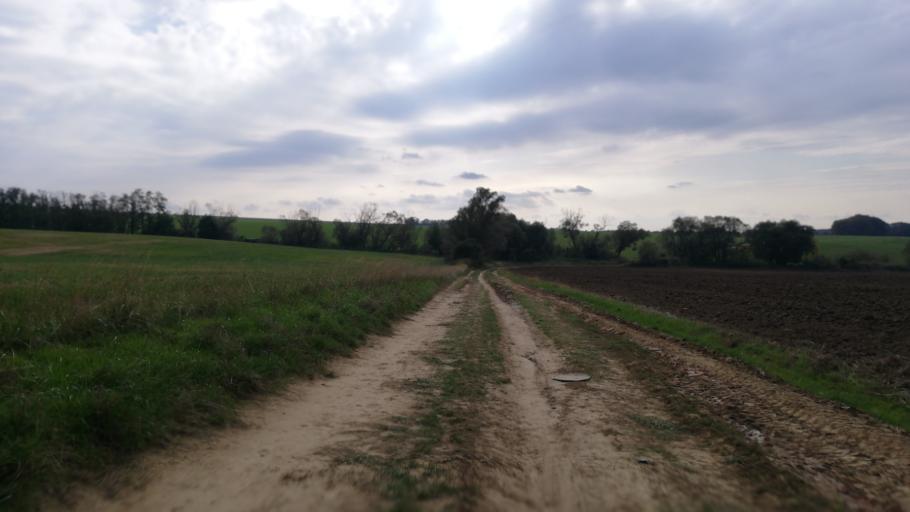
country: SK
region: Trnavsky
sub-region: Okres Skalica
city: Skalica
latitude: 48.8208
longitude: 17.2645
